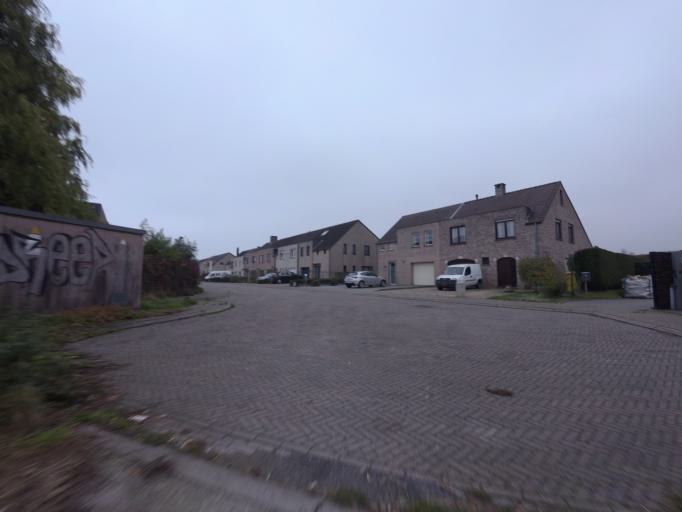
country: BE
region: Flanders
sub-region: Provincie Vlaams-Brabant
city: Diegem
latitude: 50.8674
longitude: 4.4279
